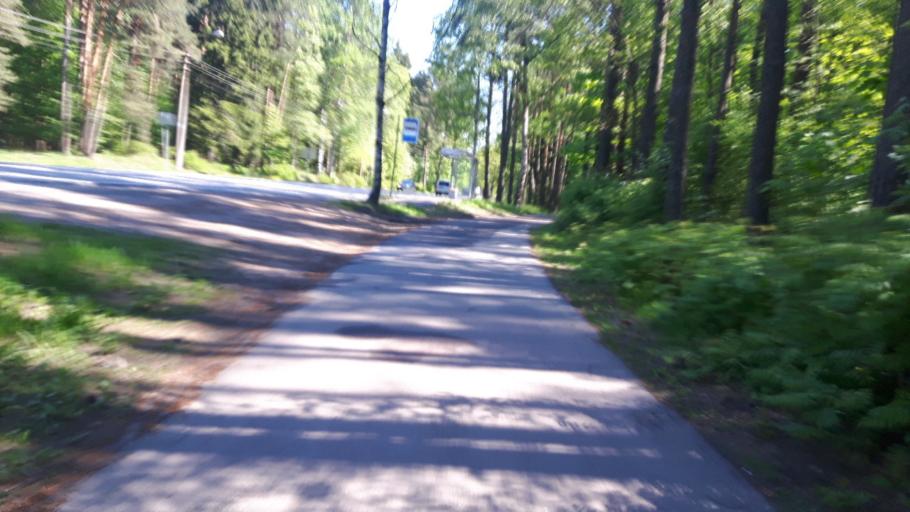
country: RU
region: St.-Petersburg
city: Zelenogorsk
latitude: 60.1924
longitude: 29.6808
